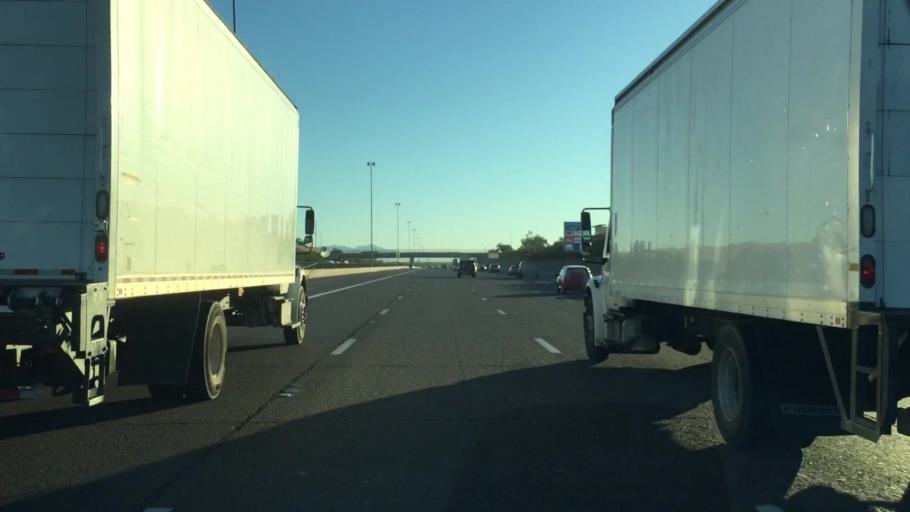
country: US
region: Arizona
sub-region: Maricopa County
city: Mesa
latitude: 33.3851
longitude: -111.8197
